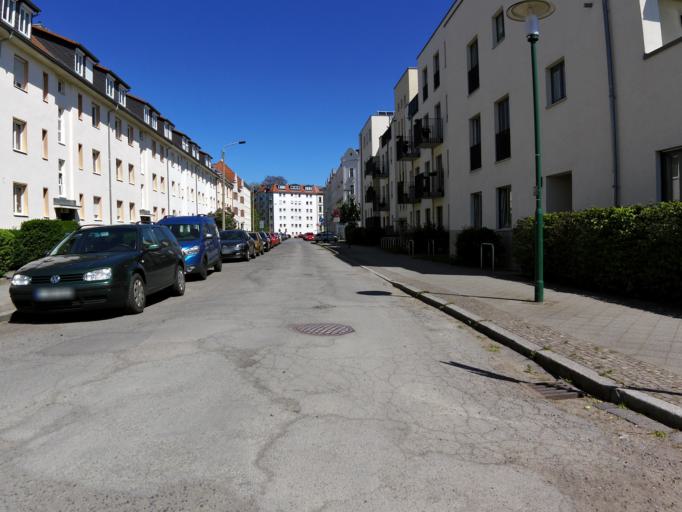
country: DE
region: Saxony
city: Leipzig
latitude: 51.3611
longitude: 12.3532
